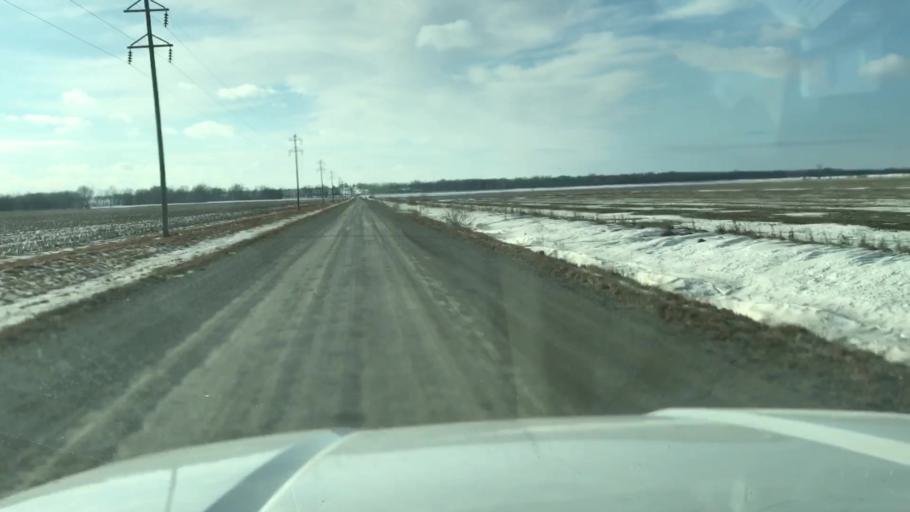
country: US
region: Missouri
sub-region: Holt County
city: Oregon
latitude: 40.1300
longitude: -95.0266
